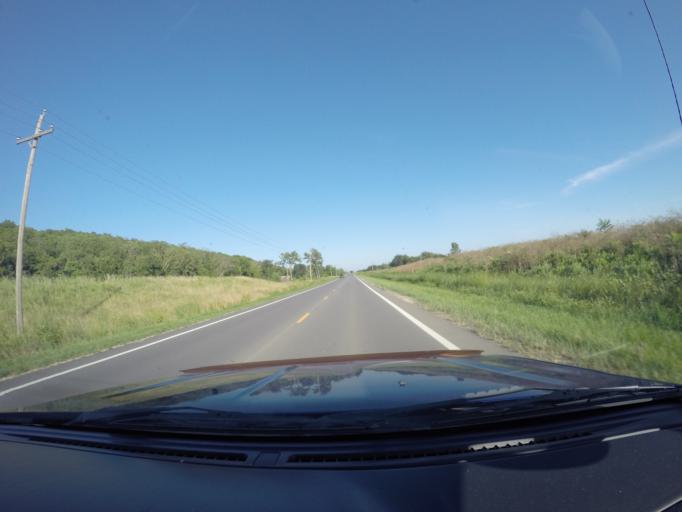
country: US
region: Kansas
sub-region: Douglas County
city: Lawrence
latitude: 39.0396
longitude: -95.2621
